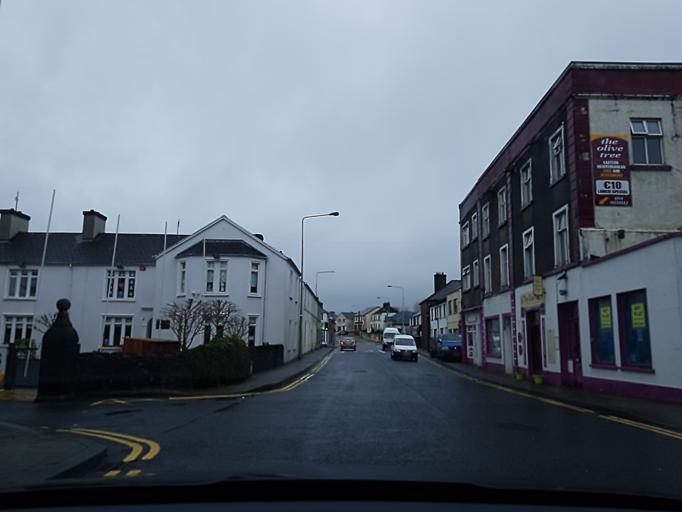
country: IE
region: Connaught
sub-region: Maigh Eo
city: Castlebar
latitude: 53.8569
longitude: -9.3014
